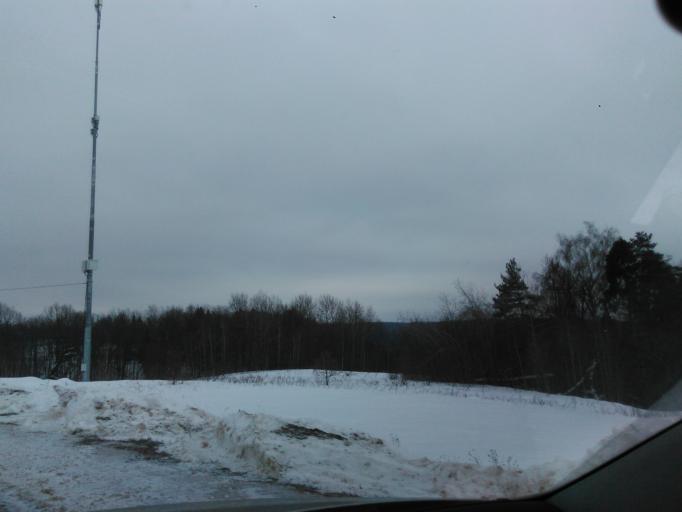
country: RU
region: Moskovskaya
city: Podosinki
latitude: 56.2753
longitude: 37.6008
